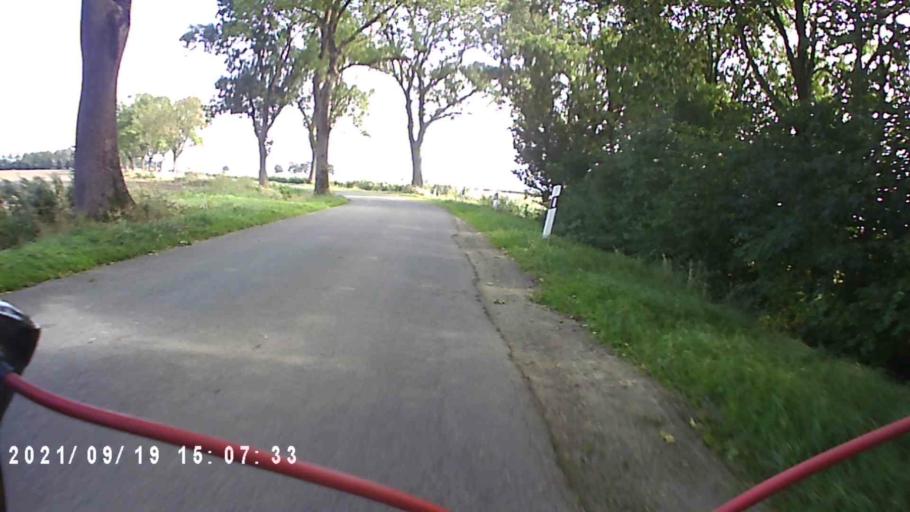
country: DE
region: Lower Saxony
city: Bunde
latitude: 53.1700
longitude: 7.2173
